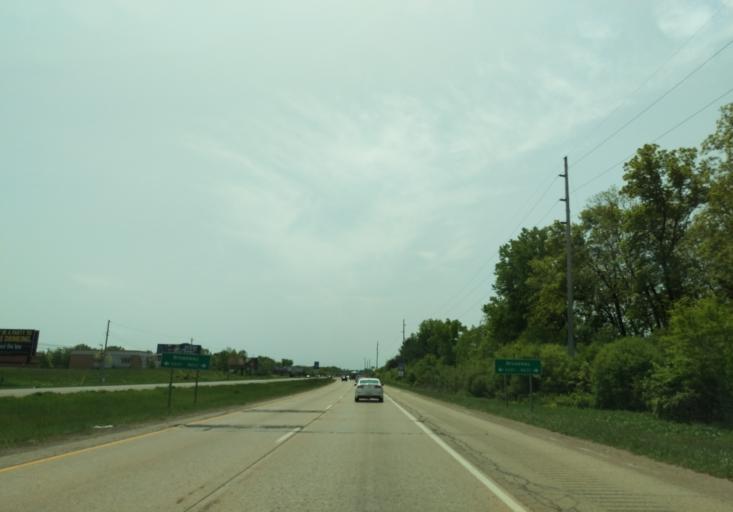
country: US
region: Wisconsin
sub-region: Dane County
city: Monona
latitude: 43.0559
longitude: -89.3093
